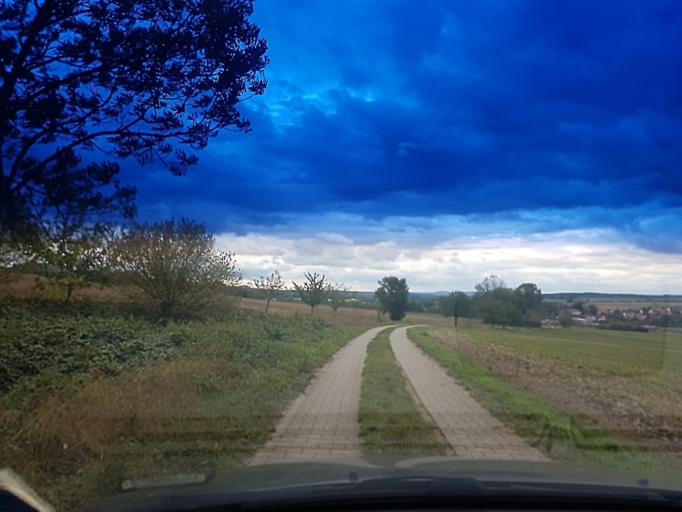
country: DE
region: Bavaria
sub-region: Upper Franconia
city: Schesslitz
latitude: 49.9930
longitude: 11.0593
